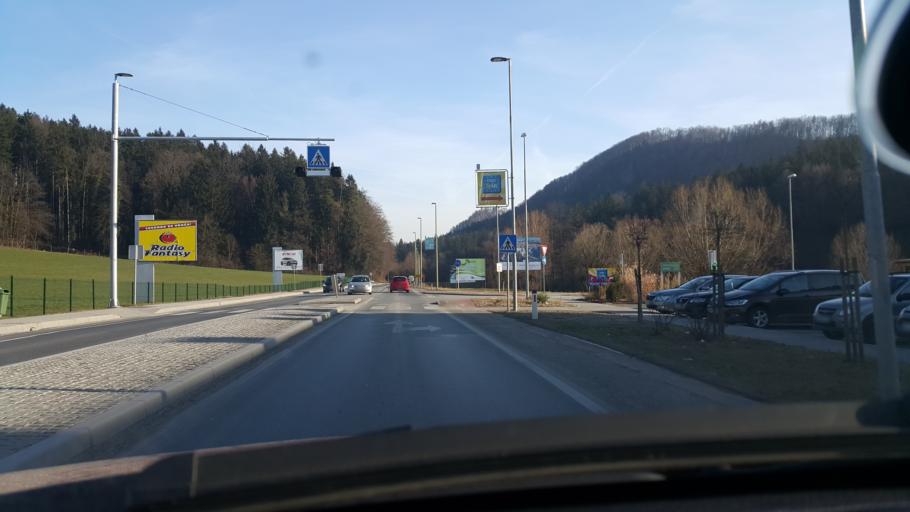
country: SI
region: Velenje
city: Velenje
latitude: 46.3555
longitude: 15.1171
